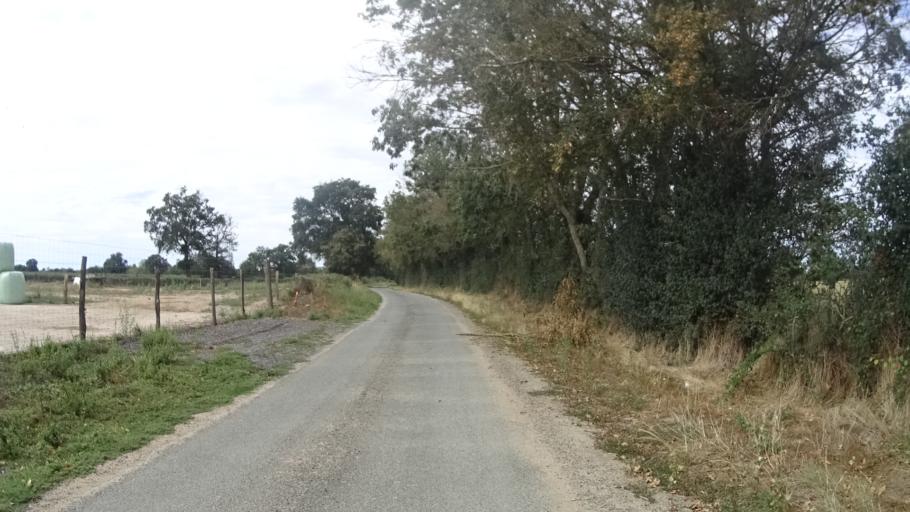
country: FR
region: Auvergne
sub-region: Departement de l'Allier
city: Beaulon
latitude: 46.6478
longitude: 3.6771
